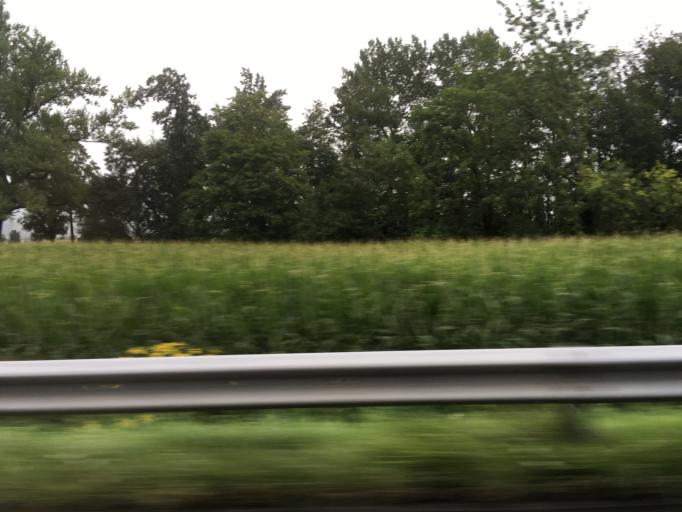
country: CH
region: Schwyz
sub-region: Bezirk March
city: Tuggen
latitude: 47.2033
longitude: 8.9666
